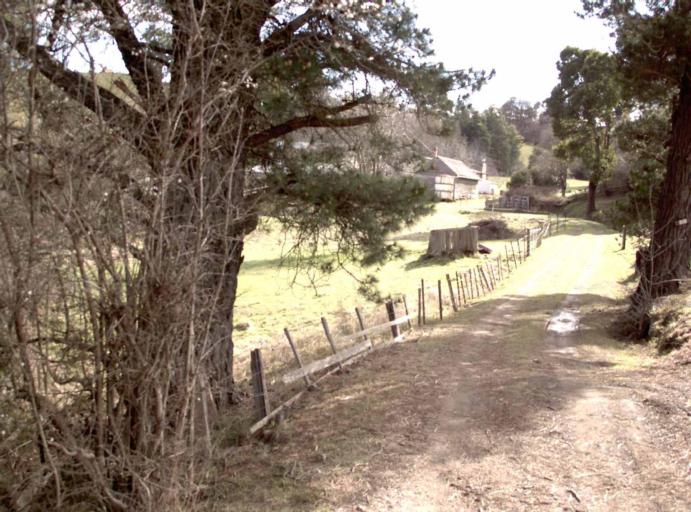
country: AU
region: Tasmania
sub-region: Launceston
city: Mayfield
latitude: -41.2468
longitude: 147.2464
